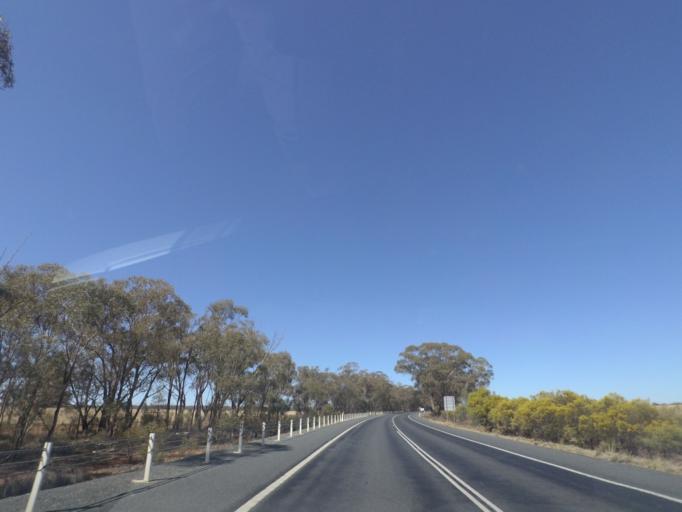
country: AU
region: New South Wales
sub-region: Bland
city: West Wyalong
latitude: -34.1136
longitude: 147.1377
